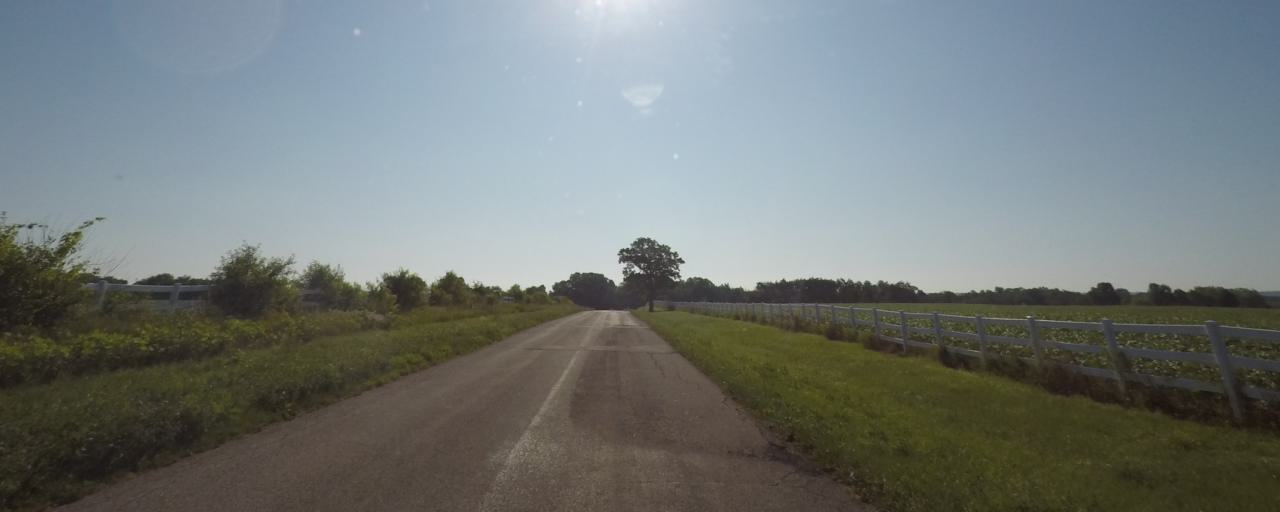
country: US
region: Wisconsin
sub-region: Jefferson County
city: Palmyra
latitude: 42.9190
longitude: -88.5514
